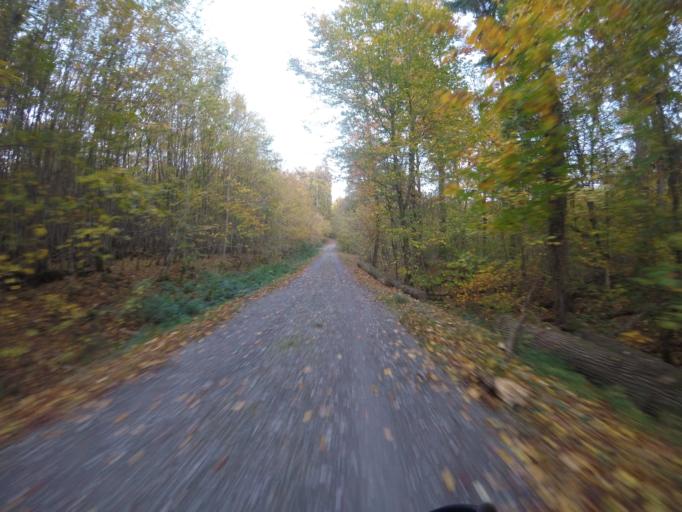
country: DE
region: Baden-Wuerttemberg
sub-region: Regierungsbezirk Stuttgart
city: Kirchberg an der Murr
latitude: 48.9818
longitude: 9.3344
